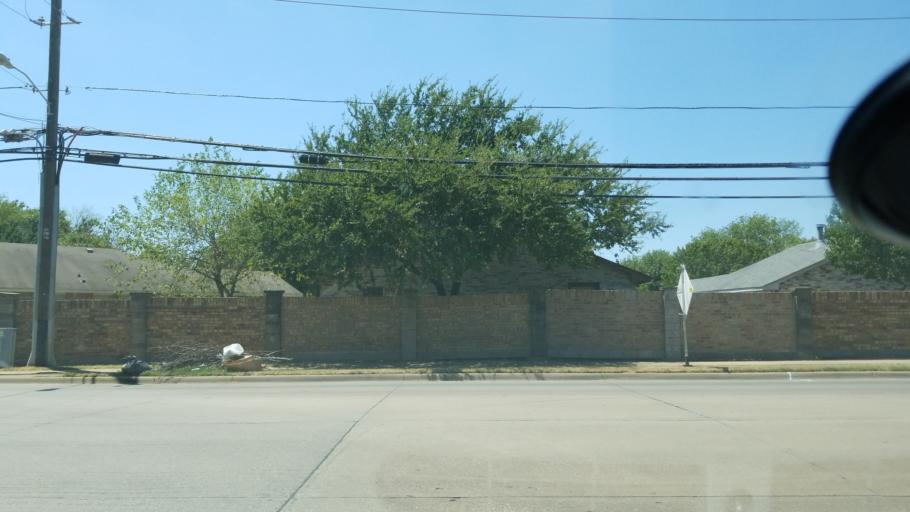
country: US
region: Texas
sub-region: Dallas County
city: Cockrell Hill
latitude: 32.7292
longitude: -96.8914
